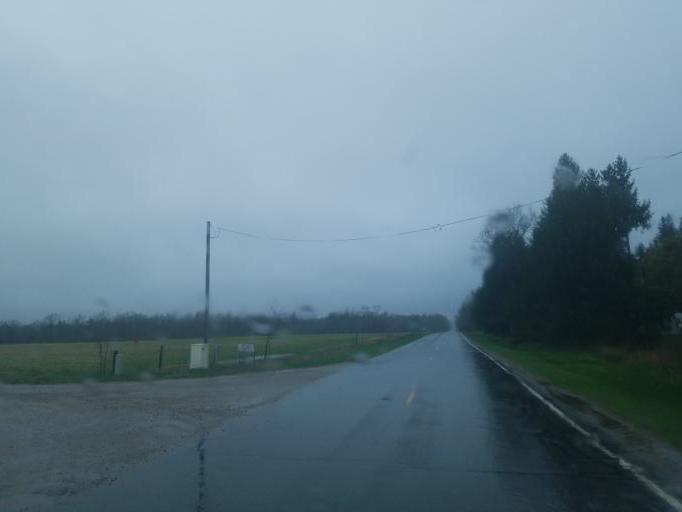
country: US
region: Michigan
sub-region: Montcalm County
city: Edmore
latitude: 43.4876
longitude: -85.0054
